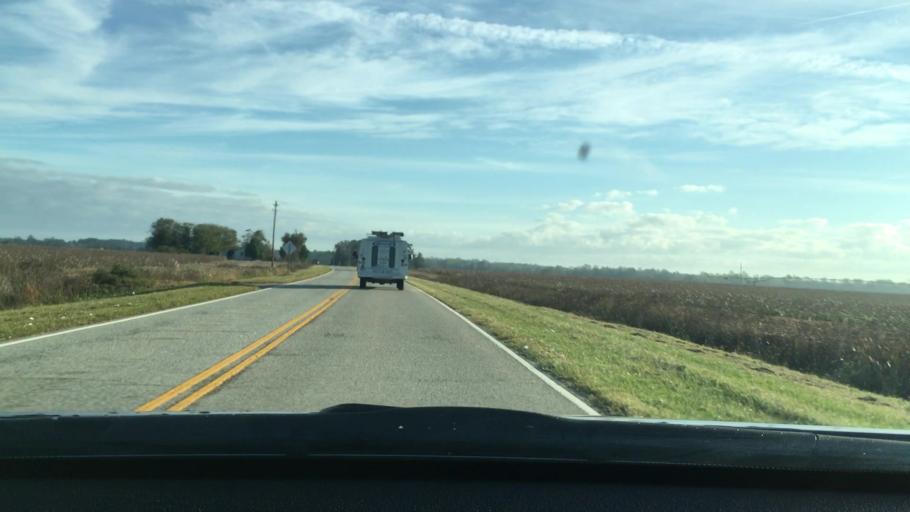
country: US
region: South Carolina
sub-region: Lee County
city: Bishopville
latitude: 34.0677
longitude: -80.2157
